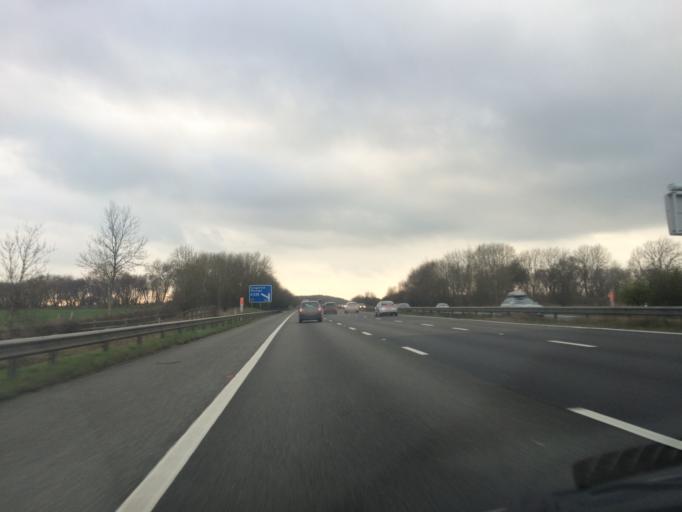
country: GB
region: England
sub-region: West Berkshire
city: Wickham
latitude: 51.4471
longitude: -1.4498
